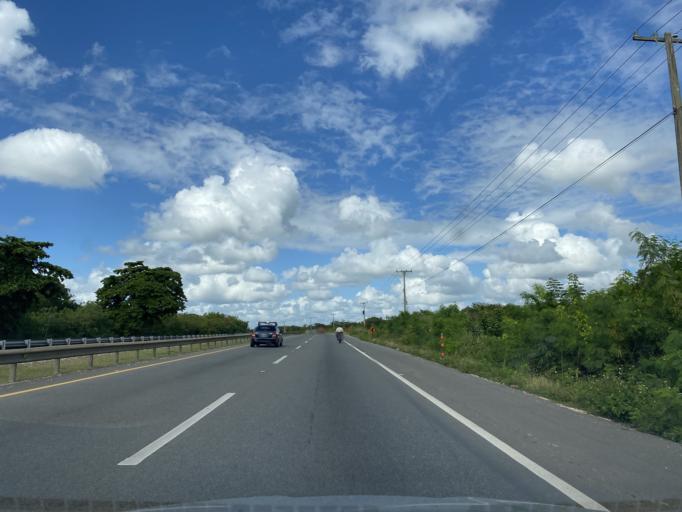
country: DO
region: Santo Domingo
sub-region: Santo Domingo
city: Boca Chica
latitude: 18.4412
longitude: -69.5811
